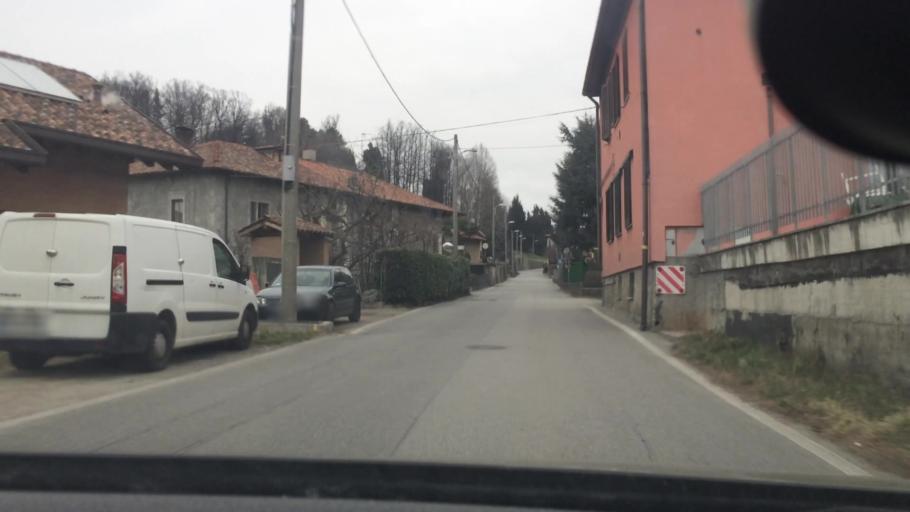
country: IT
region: Lombardy
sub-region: Provincia di Como
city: Inverigo
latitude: 45.7337
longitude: 9.2070
